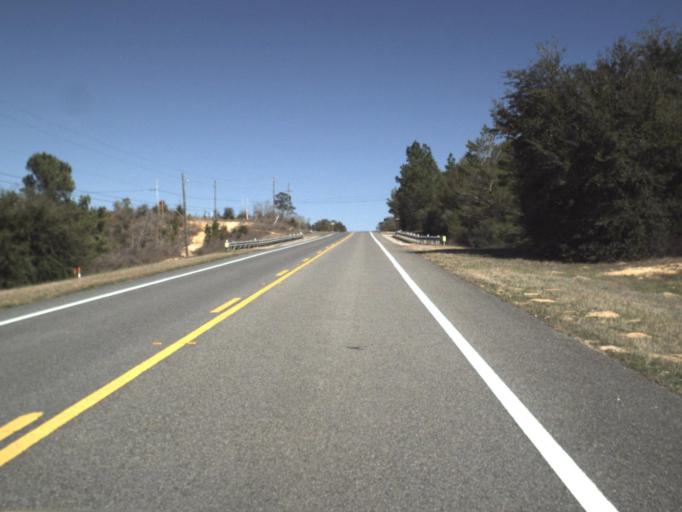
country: US
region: Florida
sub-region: Bay County
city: Youngstown
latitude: 30.4333
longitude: -85.5366
